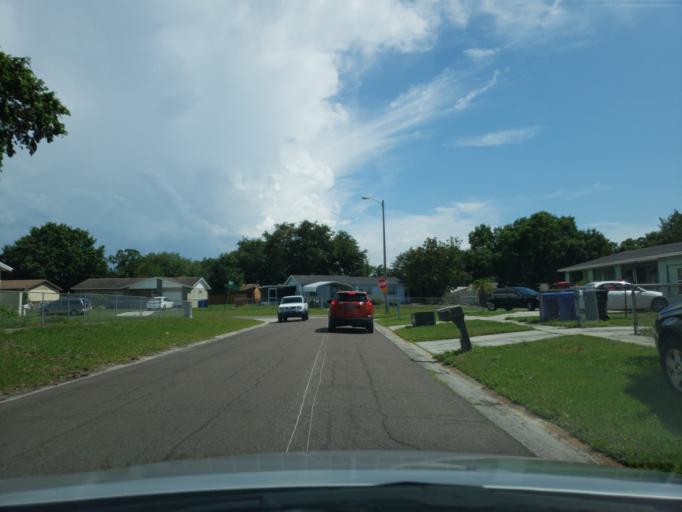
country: US
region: Florida
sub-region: Hillsborough County
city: Palm River-Clair Mel
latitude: 27.9307
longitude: -82.3762
